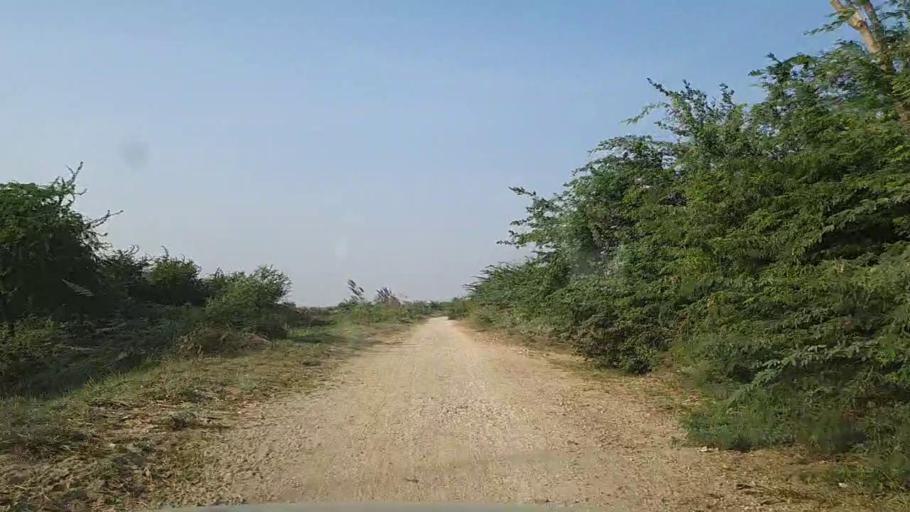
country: PK
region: Sindh
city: Mirpur Sakro
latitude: 24.5926
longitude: 67.6489
